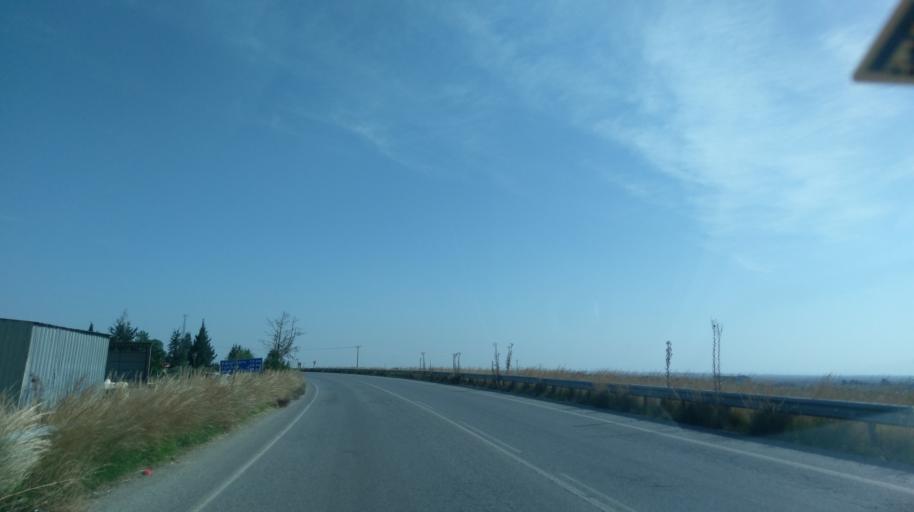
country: CY
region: Ammochostos
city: Lefkonoiko
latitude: 35.2424
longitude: 33.5998
